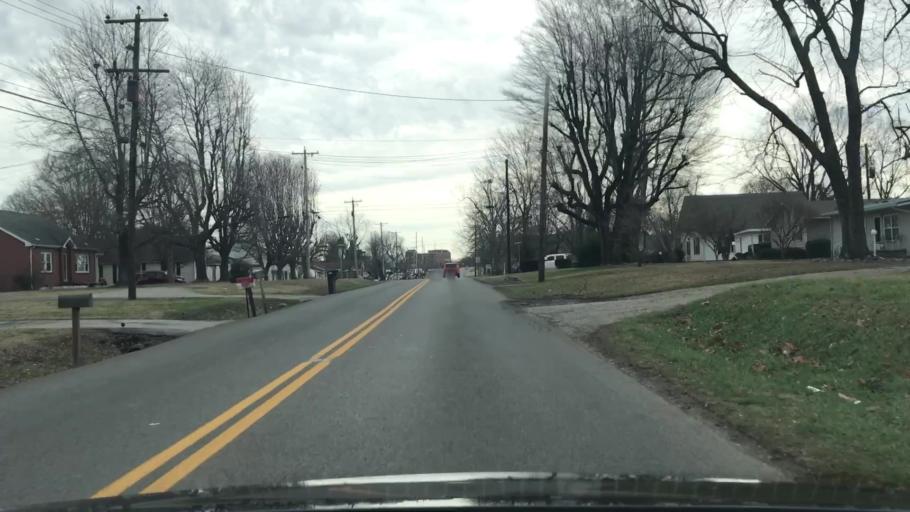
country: US
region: Kentucky
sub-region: Christian County
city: Hopkinsville
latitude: 36.8606
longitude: -87.5075
